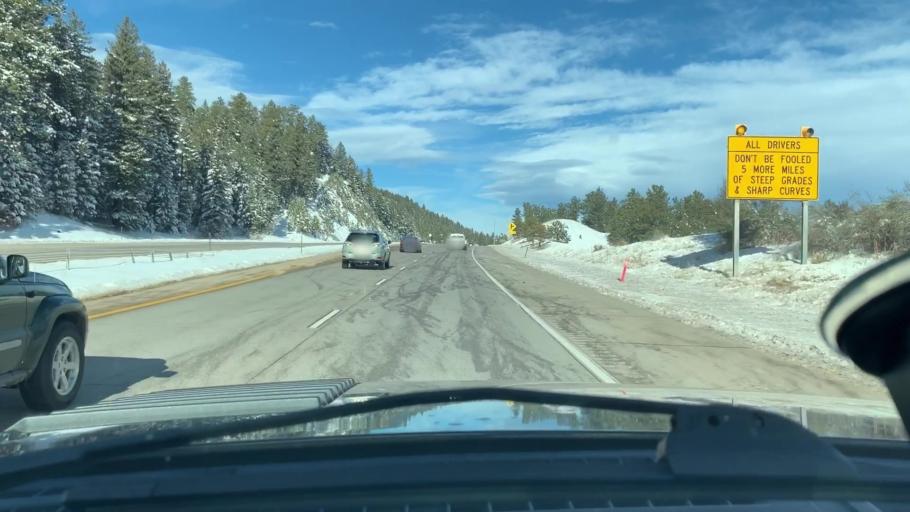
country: US
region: Colorado
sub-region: Jefferson County
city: Indian Hills
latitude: 39.5969
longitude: -105.2246
